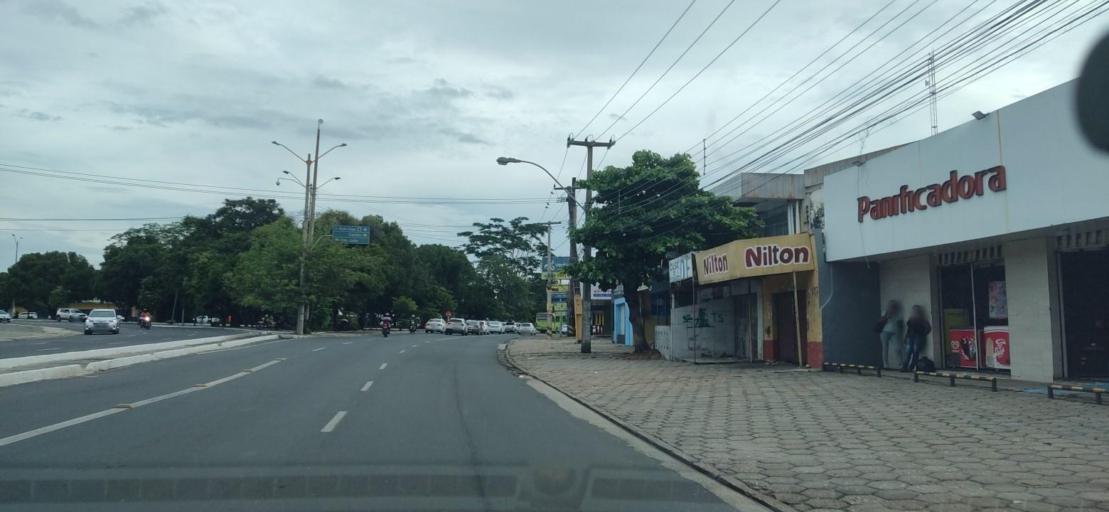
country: BR
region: Piaui
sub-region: Teresina
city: Teresina
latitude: -5.0797
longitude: -42.7747
